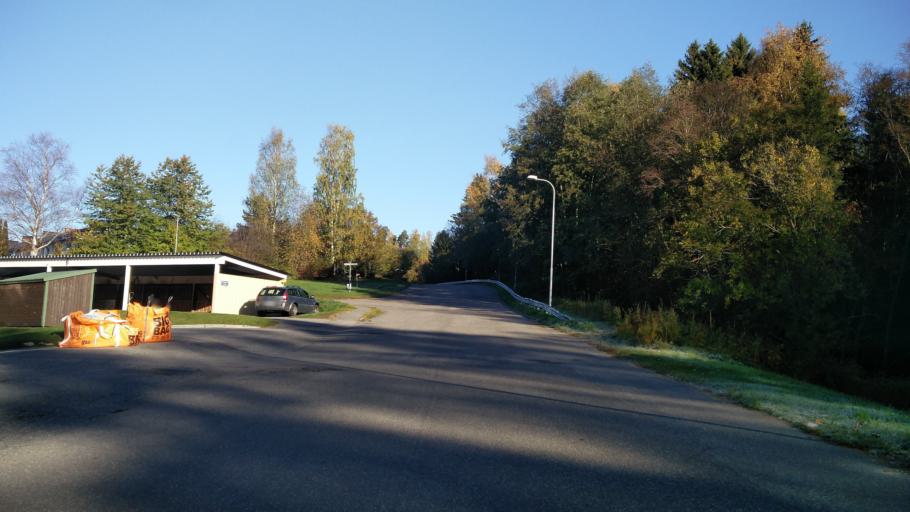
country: SE
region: Vaesternorrland
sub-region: Sundsvalls Kommun
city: Sundsvall
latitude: 62.4044
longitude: 17.2657
